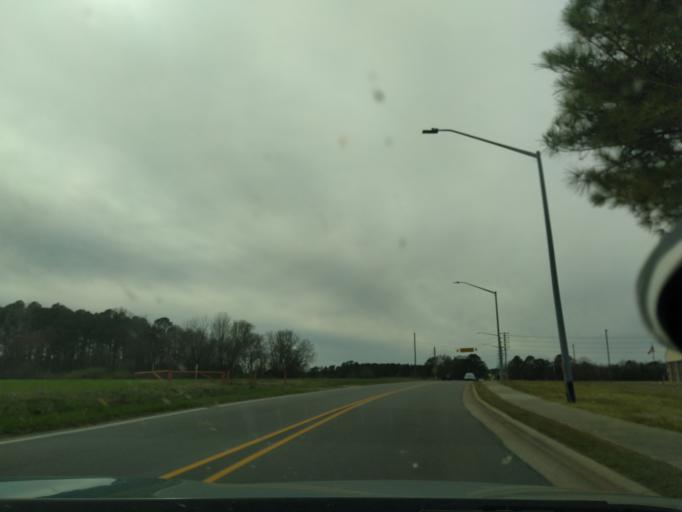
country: US
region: North Carolina
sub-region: Edgecombe County
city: Tarboro
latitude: 35.8953
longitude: -77.5729
